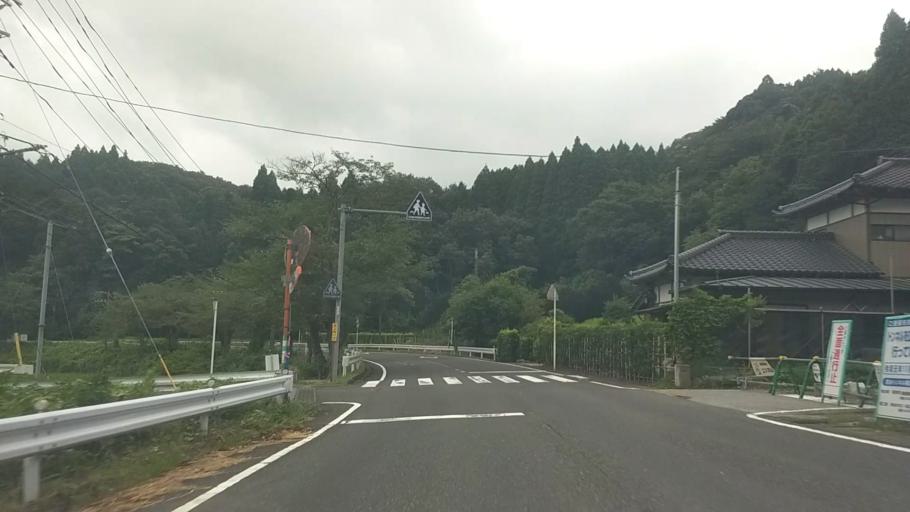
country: JP
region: Chiba
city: Kawaguchi
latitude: 35.2423
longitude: 140.0718
